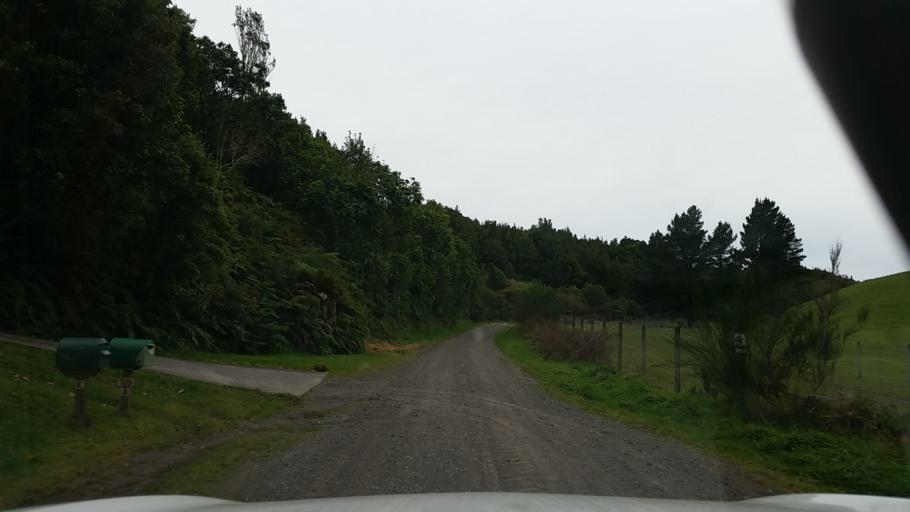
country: NZ
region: Bay of Plenty
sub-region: Rotorua District
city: Rotorua
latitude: -38.1592
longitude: 176.3690
